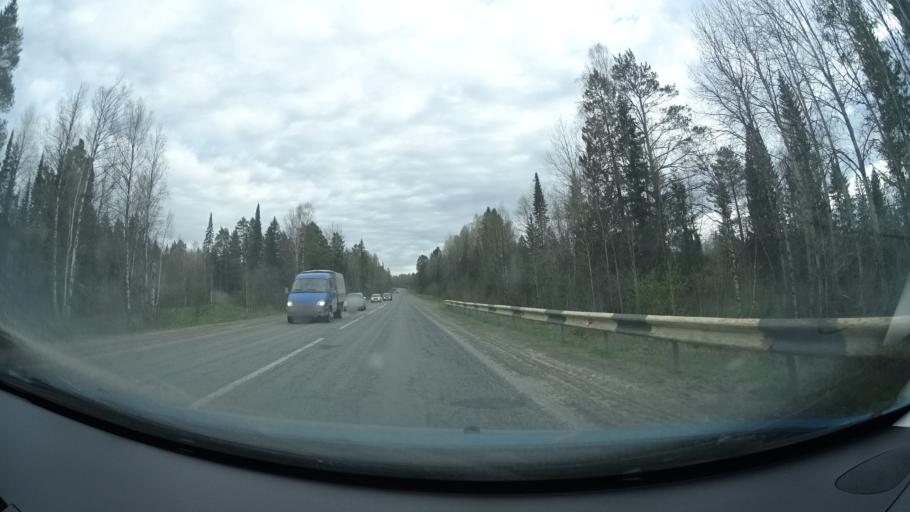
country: RU
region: Perm
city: Yugo-Kamskiy
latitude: 57.6552
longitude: 55.5971
